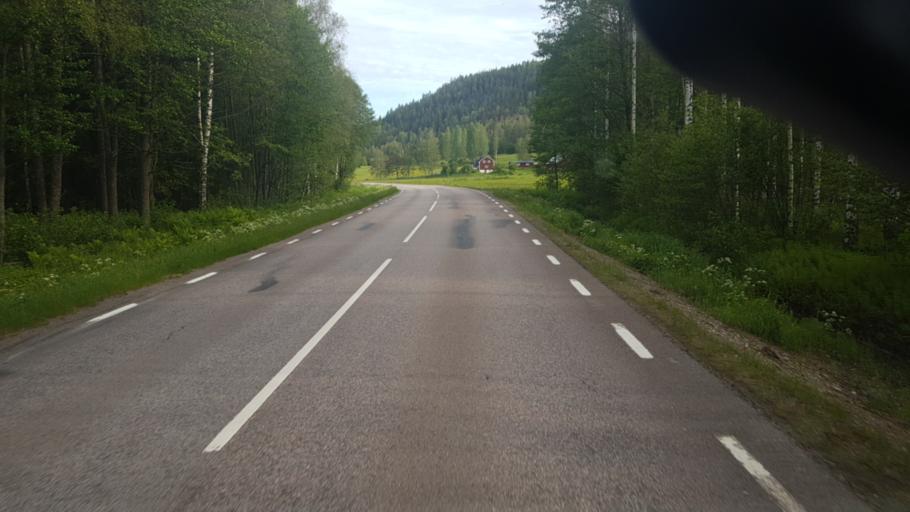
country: SE
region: Vaermland
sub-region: Arvika Kommun
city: Arvika
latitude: 59.7470
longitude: 12.6387
